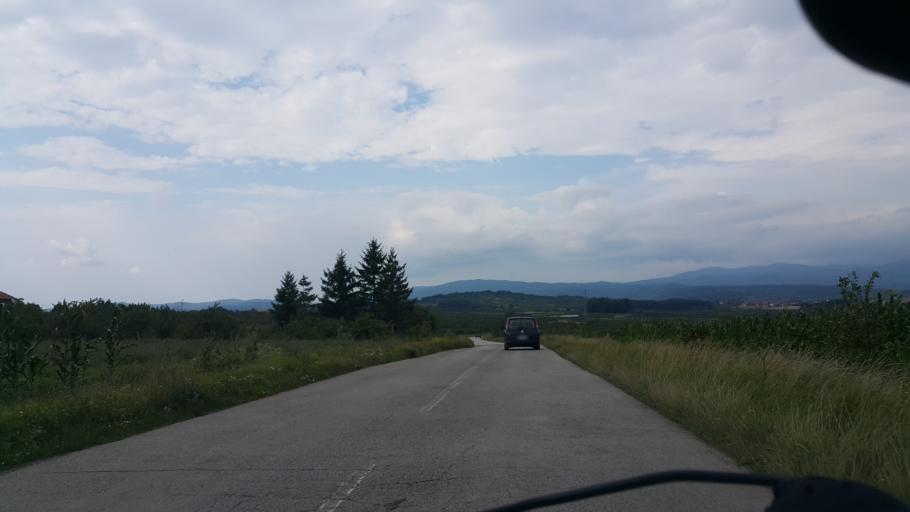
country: RS
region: Central Serbia
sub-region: Toplicki Okrug
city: Blace
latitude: 43.2687
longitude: 21.2737
